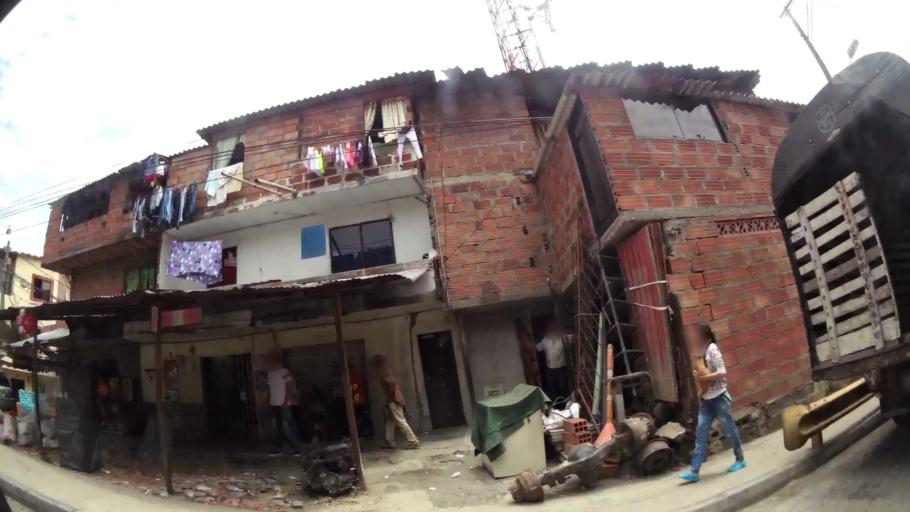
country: CO
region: Antioquia
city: Bello
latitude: 6.3079
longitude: -75.5788
